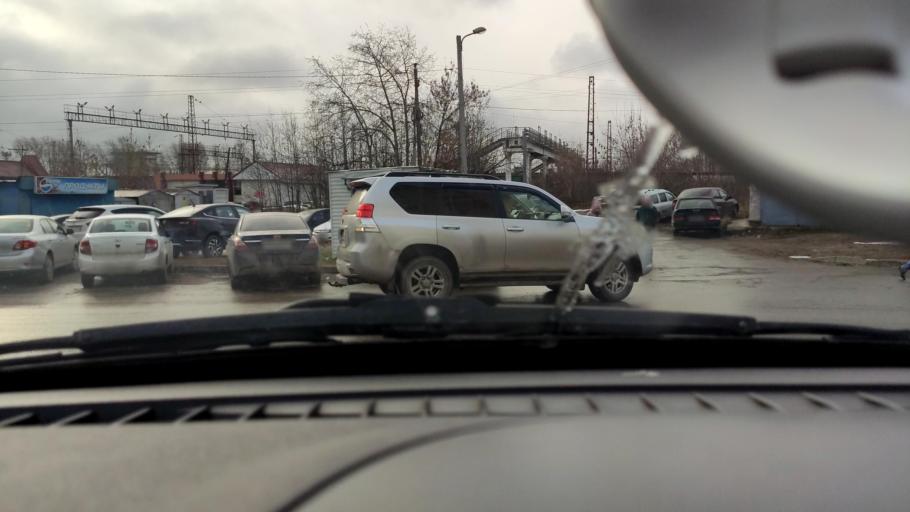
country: RU
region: Perm
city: Kondratovo
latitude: 58.0358
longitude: 56.1320
